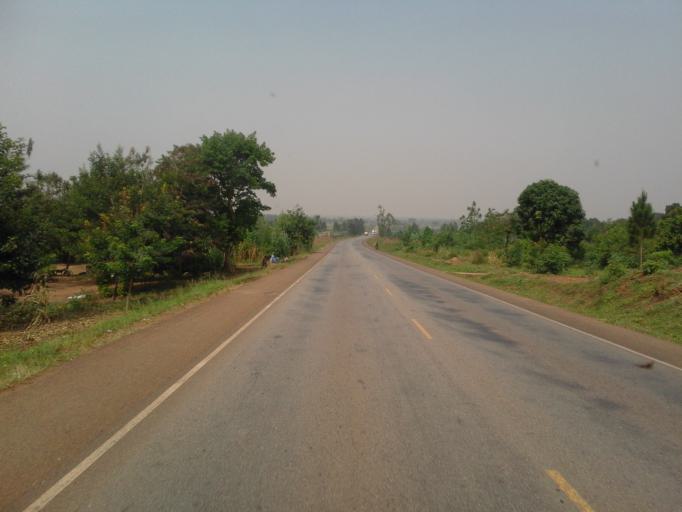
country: UG
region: Eastern Region
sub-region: Iganga District
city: Iganga
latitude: 0.6311
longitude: 33.5688
